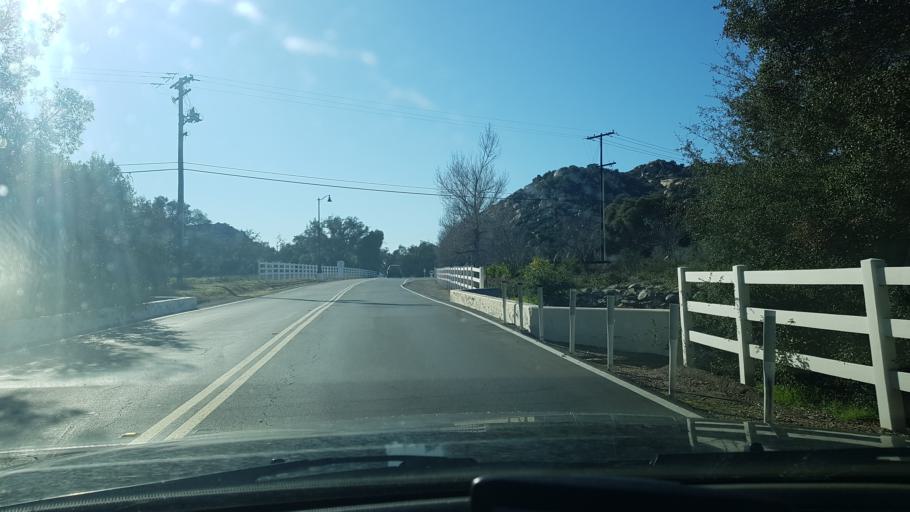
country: US
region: California
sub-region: San Diego County
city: Lakeside
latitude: 32.9330
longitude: -116.8738
